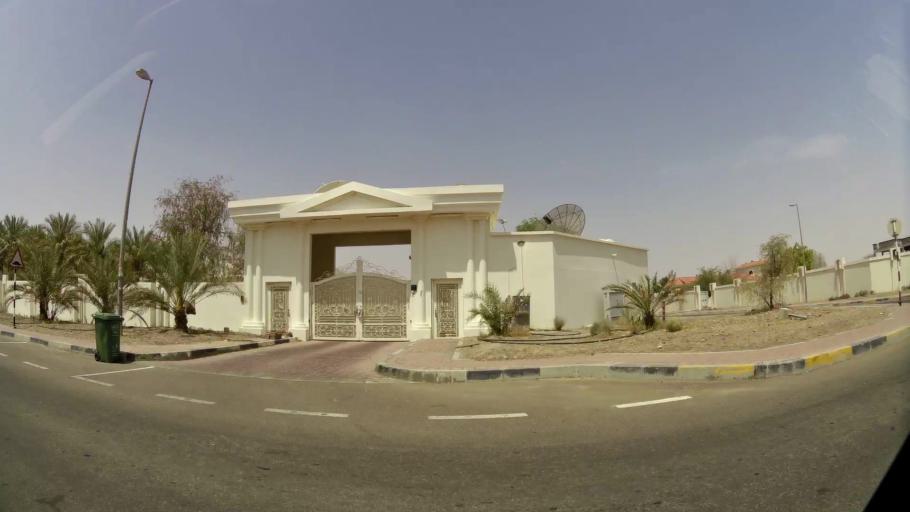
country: AE
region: Abu Dhabi
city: Al Ain
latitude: 24.1836
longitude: 55.7250
